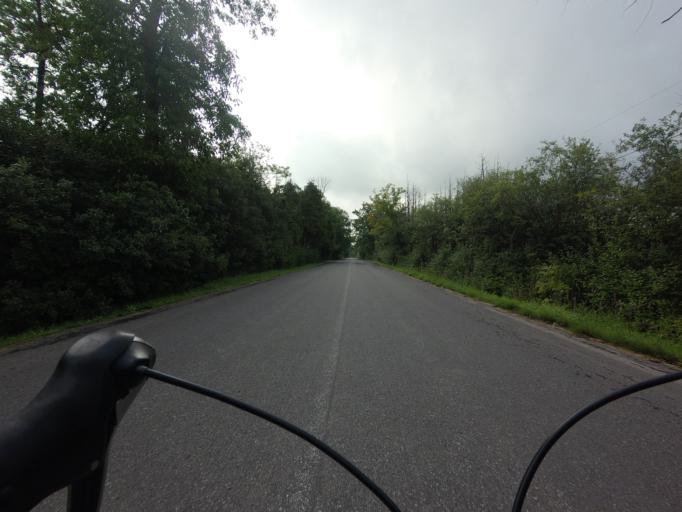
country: CA
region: Ontario
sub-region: Lanark County
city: Smiths Falls
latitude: 44.9593
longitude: -75.8039
